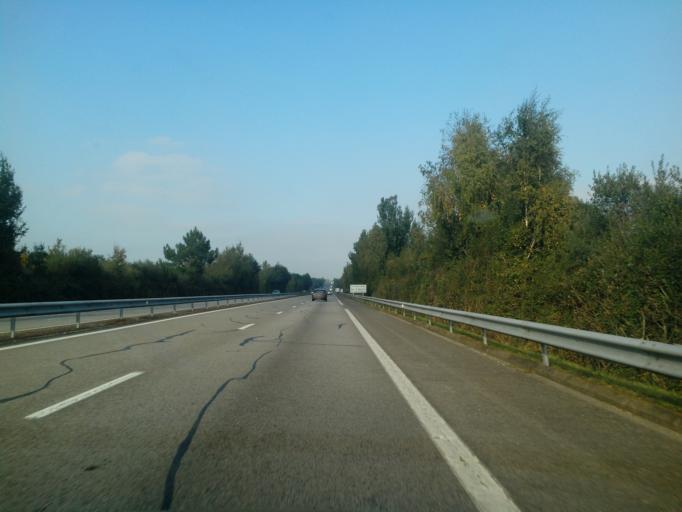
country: FR
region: Brittany
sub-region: Departement du Morbihan
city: Malestroit
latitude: 47.8356
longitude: -2.4285
